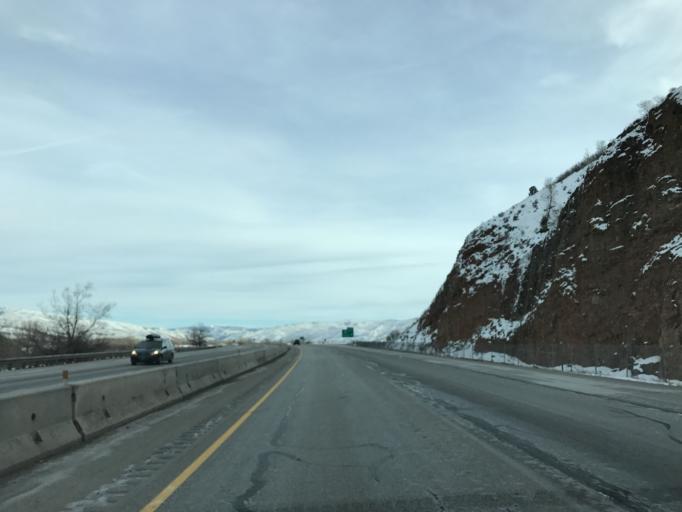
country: US
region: Utah
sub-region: Morgan County
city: Morgan
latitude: 41.0484
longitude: -111.5274
